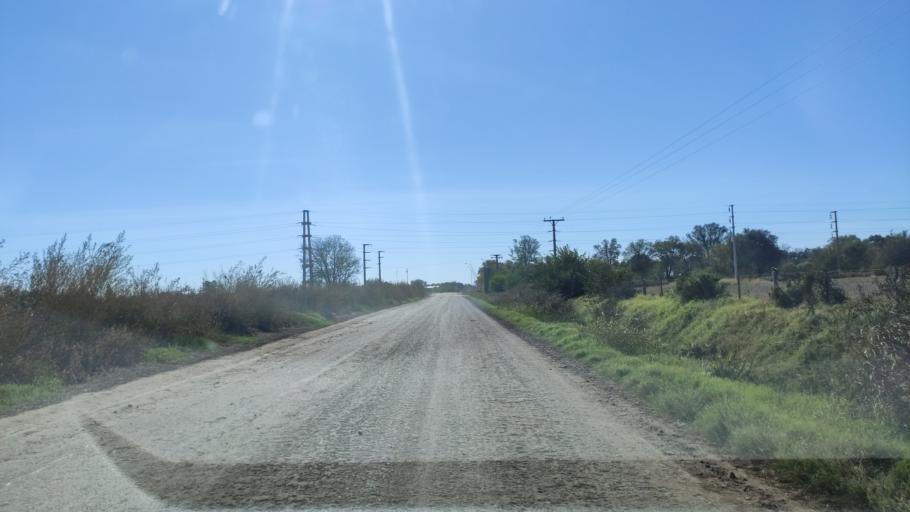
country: AR
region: Cordoba
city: Leones
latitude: -32.6642
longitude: -62.3114
